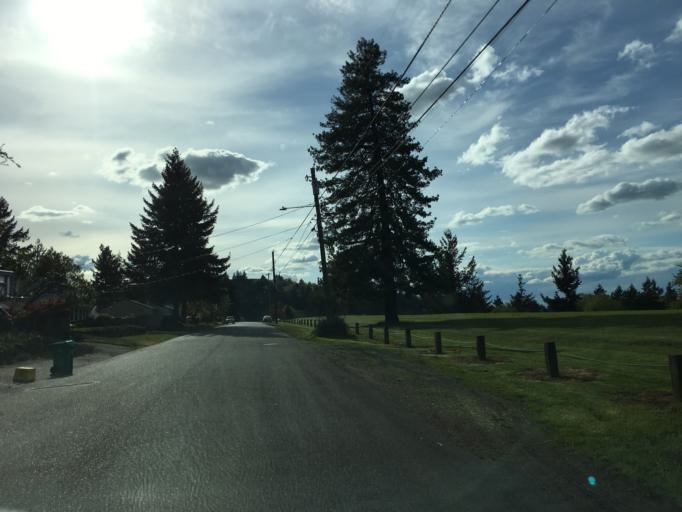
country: US
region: Oregon
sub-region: Multnomah County
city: Lents
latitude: 45.5468
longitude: -122.5497
